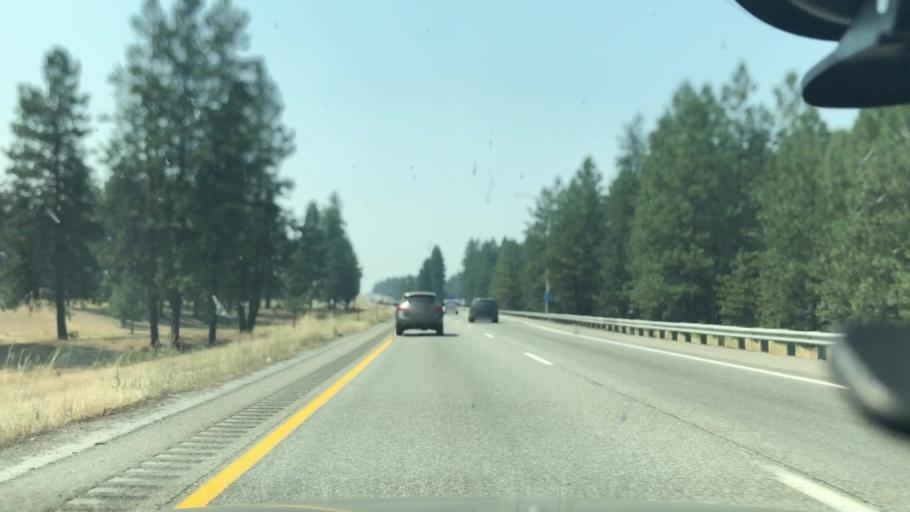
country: US
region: Idaho
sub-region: Kootenai County
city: Coeur d'Alene
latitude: 47.7091
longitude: -116.8598
